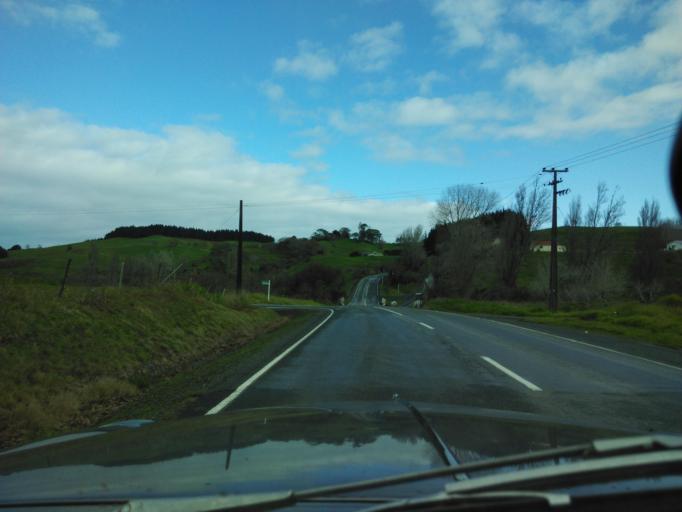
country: NZ
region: Auckland
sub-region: Auckland
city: Wellsford
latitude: -36.2841
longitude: 174.4468
